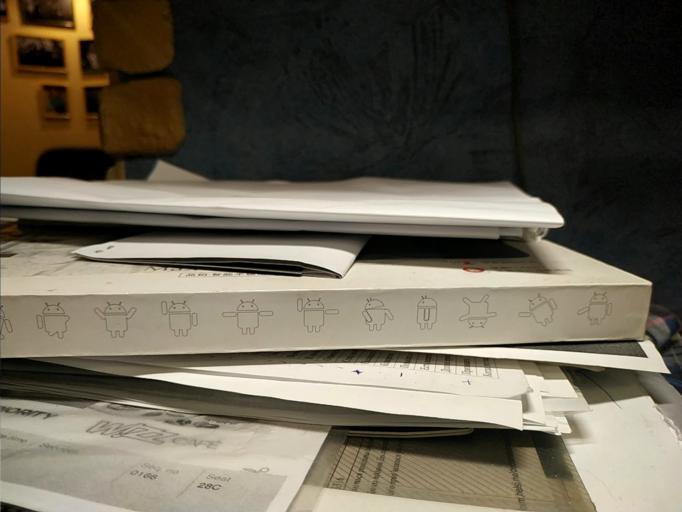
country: RU
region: Tverskaya
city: Zubtsov
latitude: 56.0798
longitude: 34.8048
